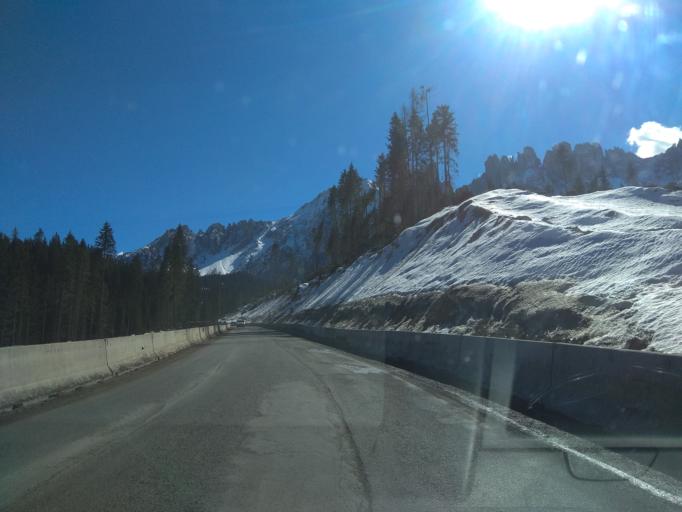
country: IT
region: Trentino-Alto Adige
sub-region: Bolzano
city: Nova Levante
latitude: 46.4121
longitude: 11.5690
